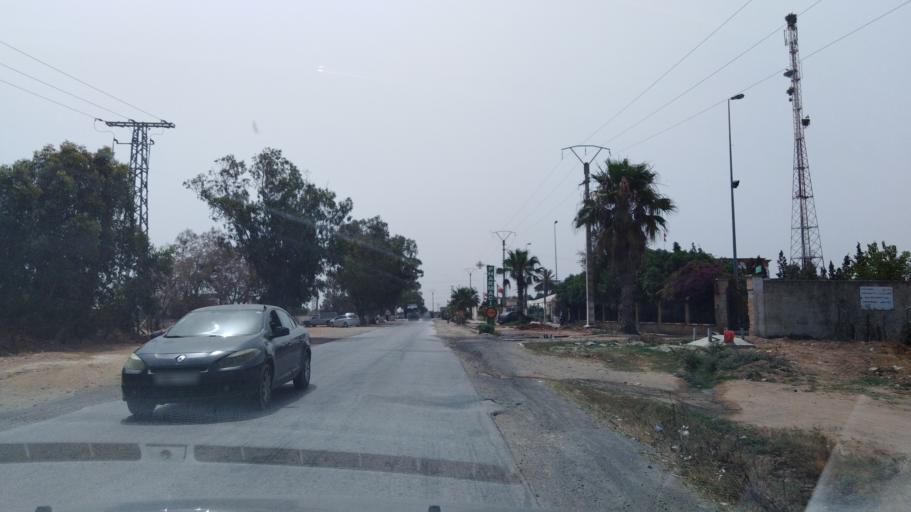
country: MA
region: Grand Casablanca
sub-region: Nouaceur
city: Bouskoura
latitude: 33.3685
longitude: -7.7782
